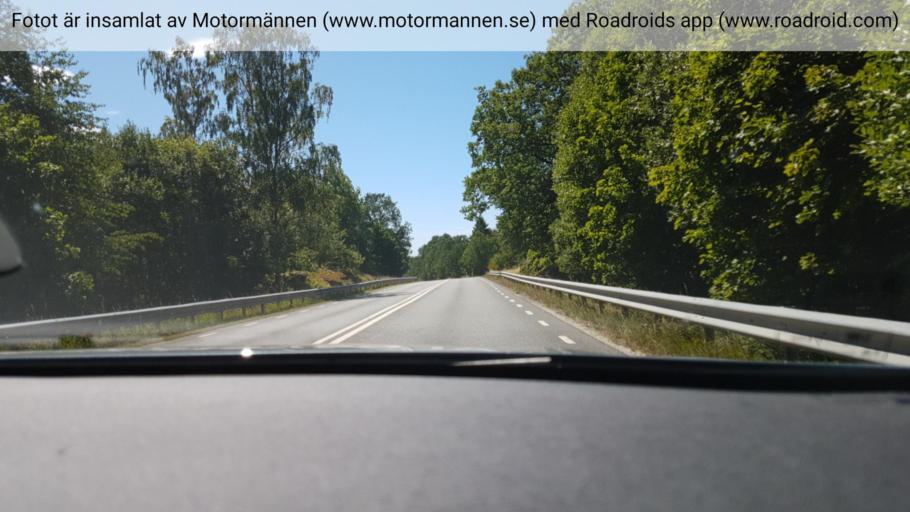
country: SE
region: Joenkoeping
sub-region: Jonkopings Kommun
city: Asa
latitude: 58.0081
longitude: 14.6296
